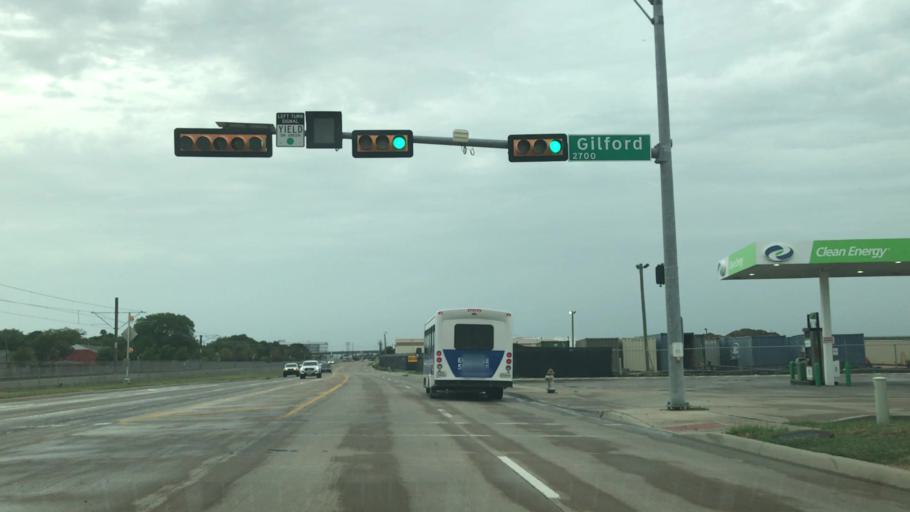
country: US
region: Texas
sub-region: Dallas County
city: University Park
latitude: 32.8392
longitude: -96.8530
